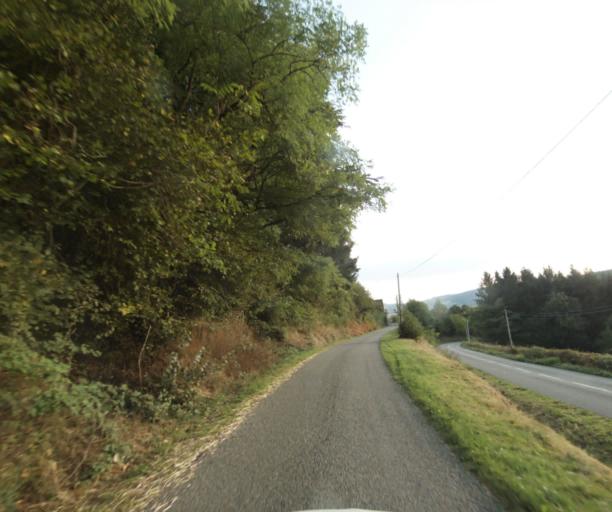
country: FR
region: Bourgogne
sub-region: Departement de Saone-et-Loire
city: Charolles
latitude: 46.3983
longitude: 4.3974
